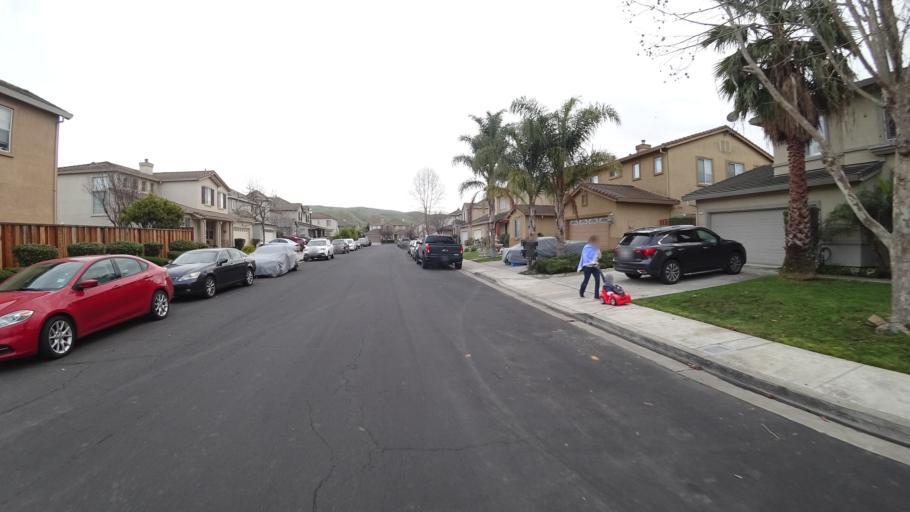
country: US
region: California
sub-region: Alameda County
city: Union City
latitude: 37.6211
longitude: -122.0470
